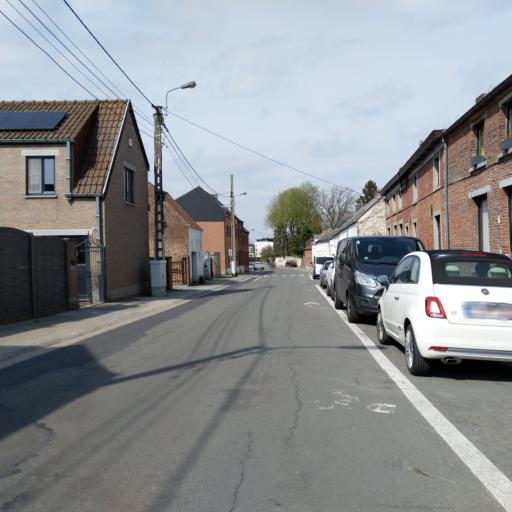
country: BE
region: Wallonia
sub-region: Province du Hainaut
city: Mons
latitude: 50.4410
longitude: 3.9625
